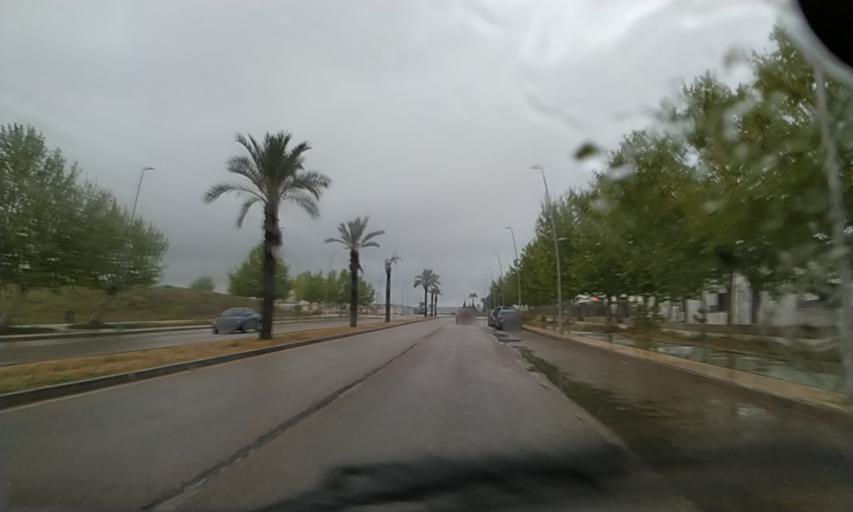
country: ES
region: Extremadura
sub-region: Provincia de Badajoz
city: Merida
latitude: 38.9140
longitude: -6.3640
